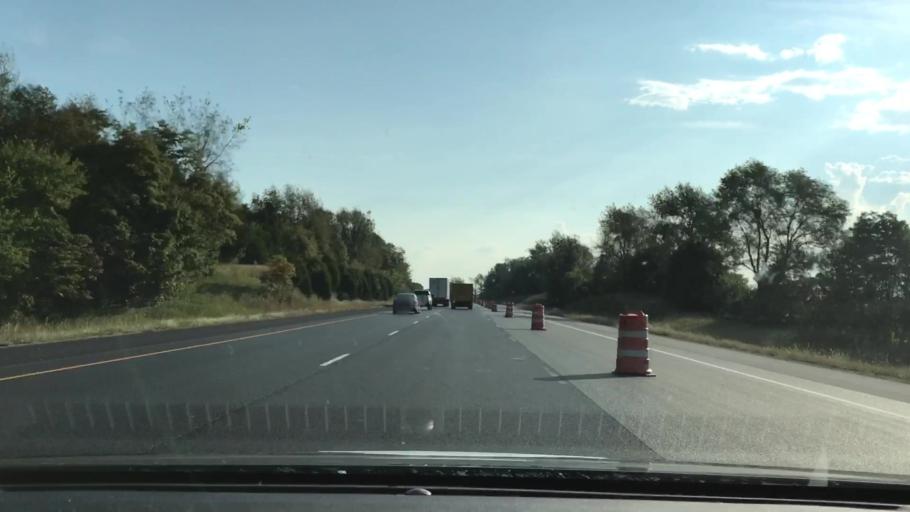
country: US
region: Kentucky
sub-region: Edmonson County
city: Brownsville
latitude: 37.0495
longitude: -86.1452
